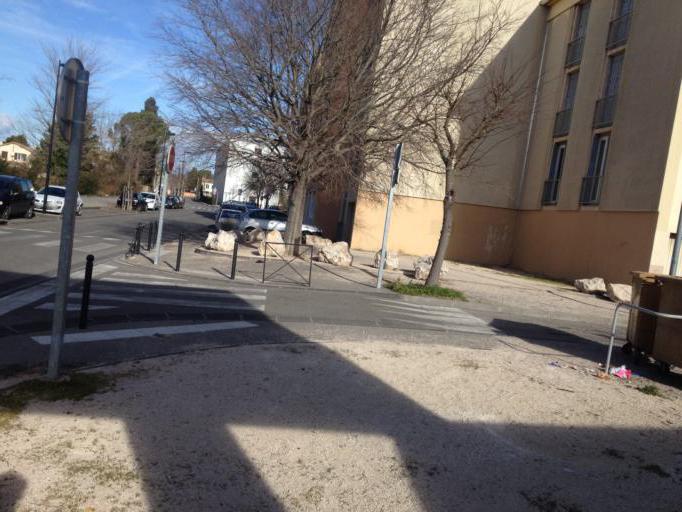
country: FR
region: Provence-Alpes-Cote d'Azur
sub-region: Departement du Vaucluse
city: Orange
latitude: 44.1303
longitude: 4.8000
